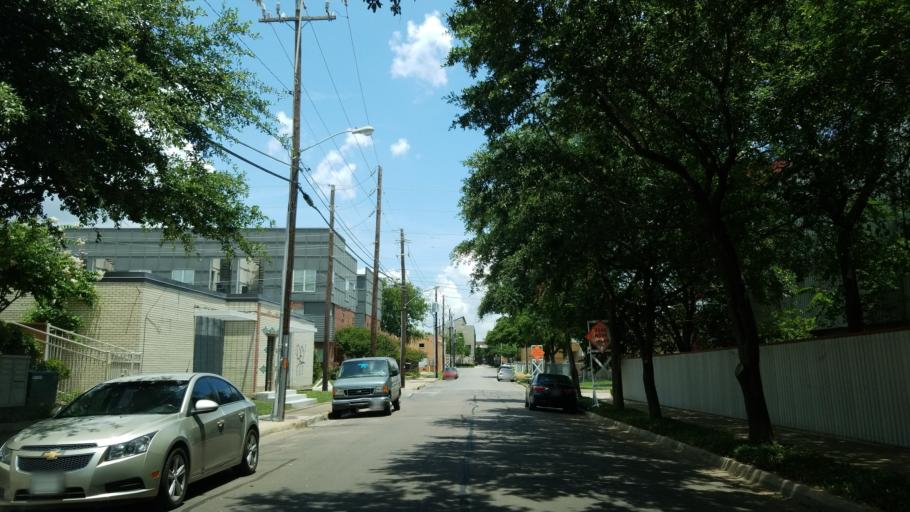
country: US
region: Texas
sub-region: Dallas County
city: Dallas
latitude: 32.7978
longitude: -96.7845
